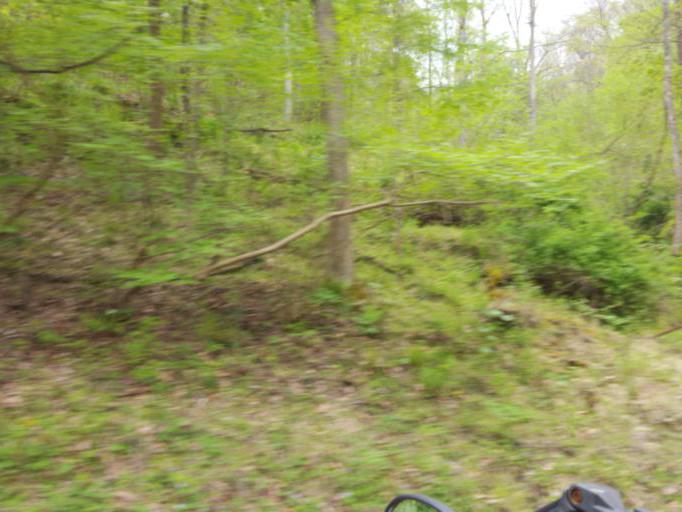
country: US
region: Ohio
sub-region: Ashland County
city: Loudonville
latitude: 40.5770
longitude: -82.1897
